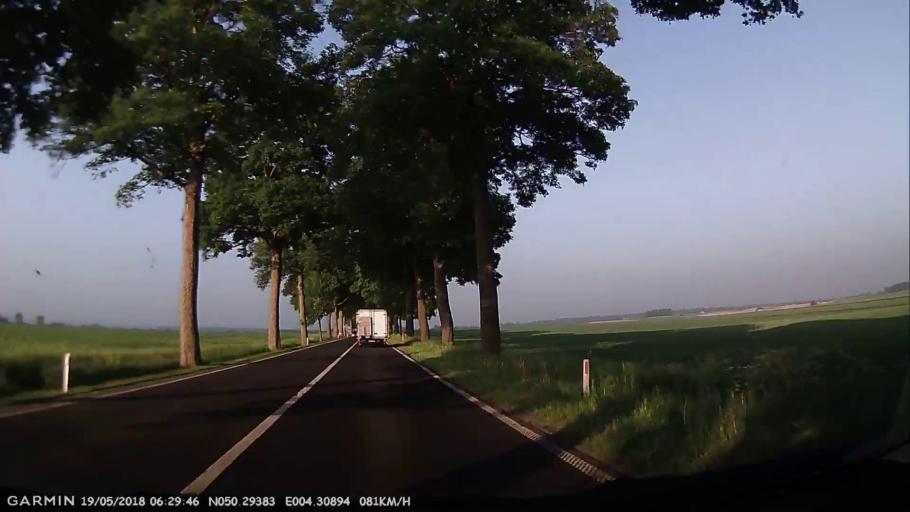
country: BE
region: Wallonia
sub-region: Province du Hainaut
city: Thuin
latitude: 50.2938
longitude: 4.3089
